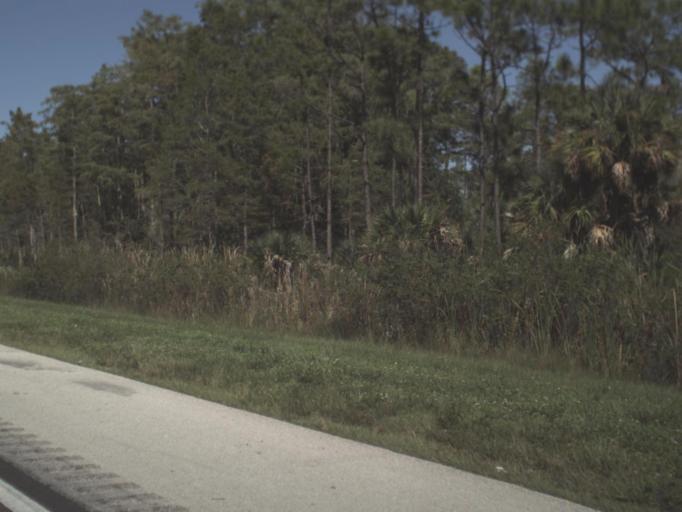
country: US
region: Florida
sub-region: Lee County
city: Fort Myers
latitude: 26.6003
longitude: -81.7994
